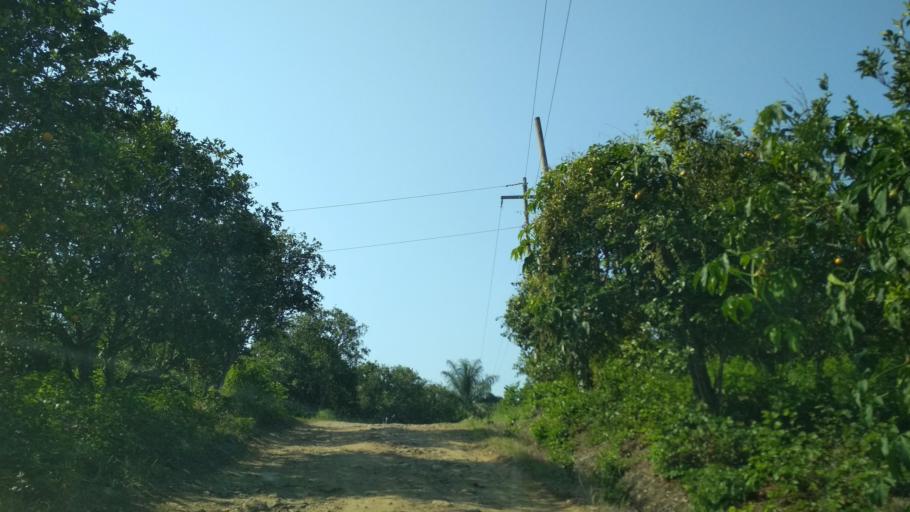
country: MX
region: Puebla
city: San Jose Acateno
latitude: 20.1729
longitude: -97.1741
